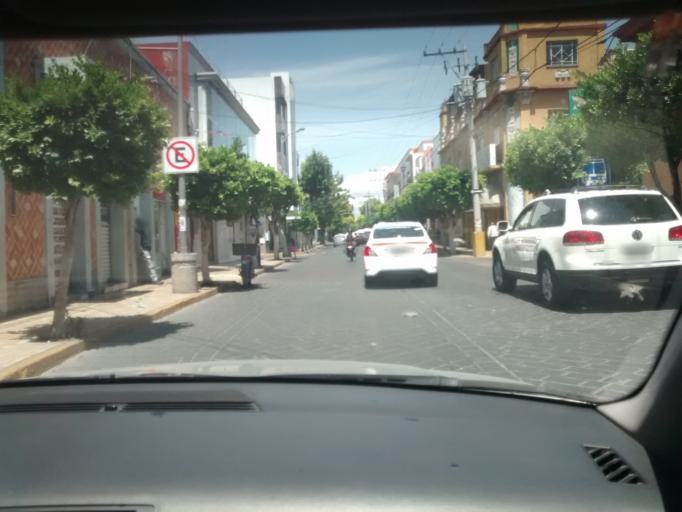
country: MX
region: Puebla
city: Tehuacan
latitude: 18.4609
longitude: -97.3931
